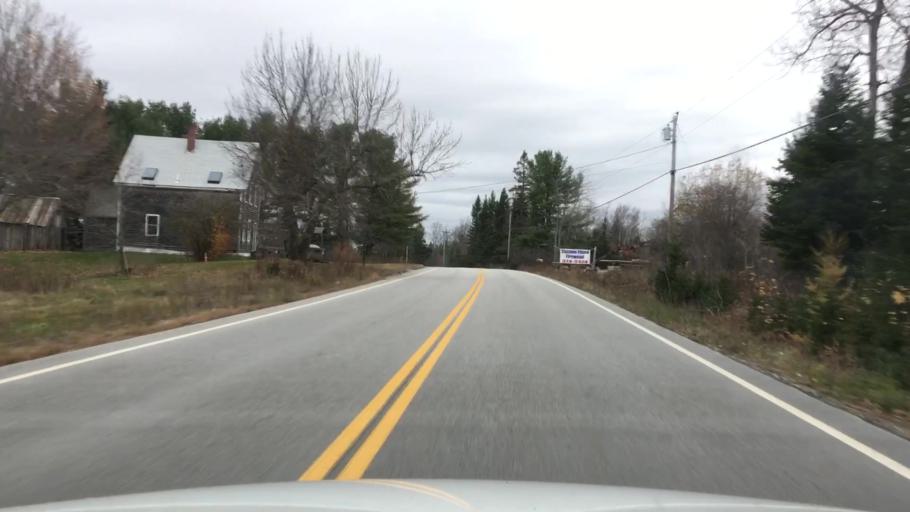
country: US
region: Maine
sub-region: Hancock County
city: Penobscot
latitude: 44.4937
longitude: -68.6446
